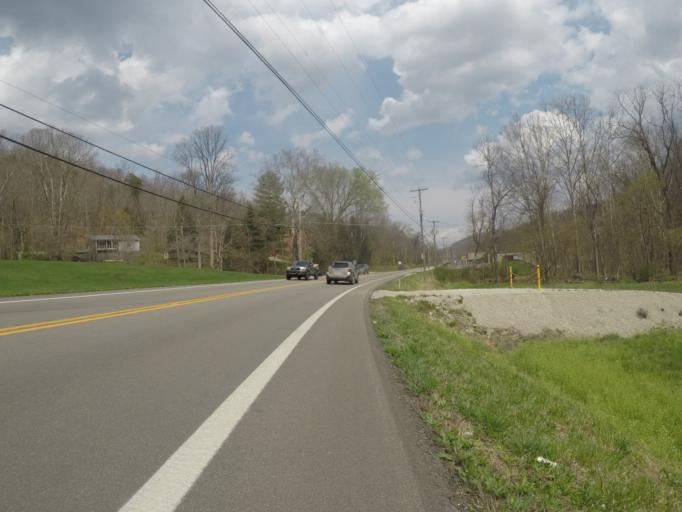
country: US
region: West Virginia
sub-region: Cabell County
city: Pea Ridge
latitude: 38.3843
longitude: -82.3340
